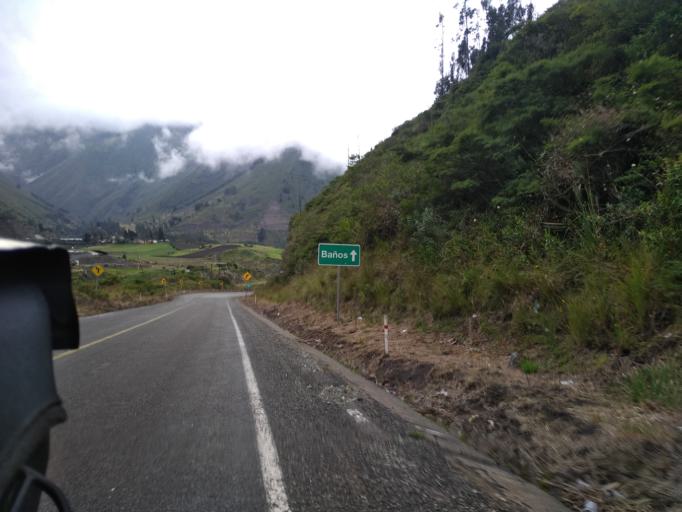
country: EC
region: Tungurahua
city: Banos
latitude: -1.5075
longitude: -78.5194
